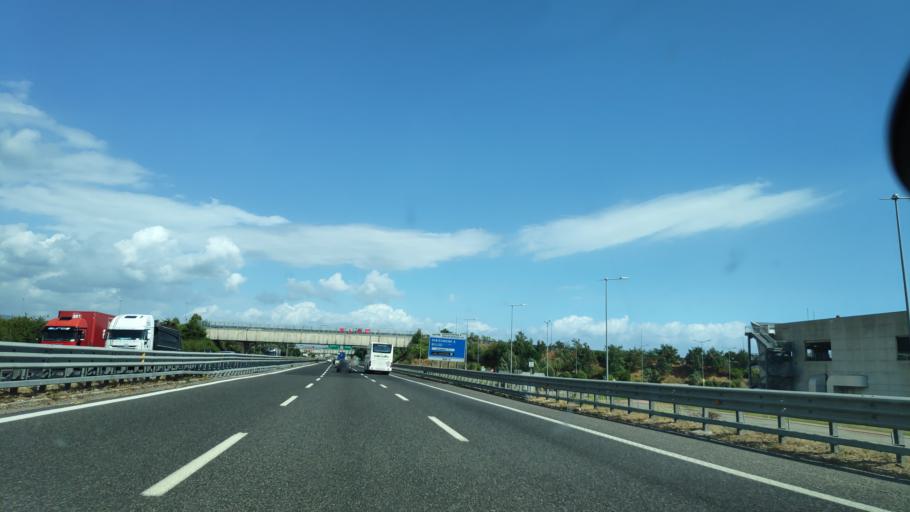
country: IT
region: Campania
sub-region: Provincia di Salerno
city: Pagliarone
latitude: 40.6369
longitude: 14.9087
